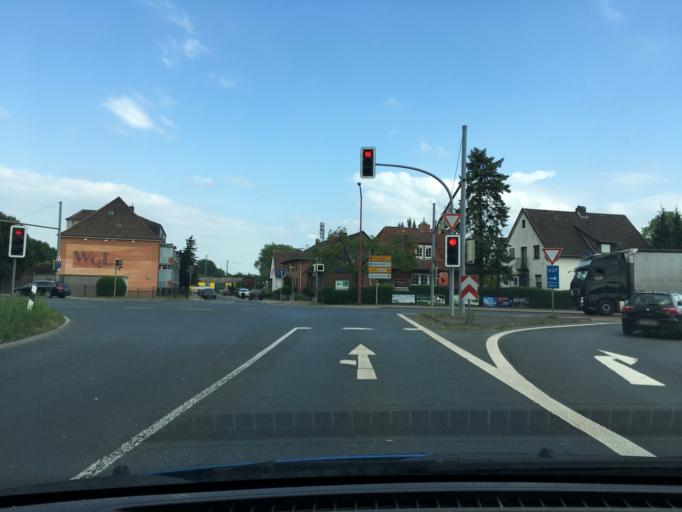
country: DE
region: Lower Saxony
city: Lehrte
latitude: 52.3886
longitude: 9.9699
